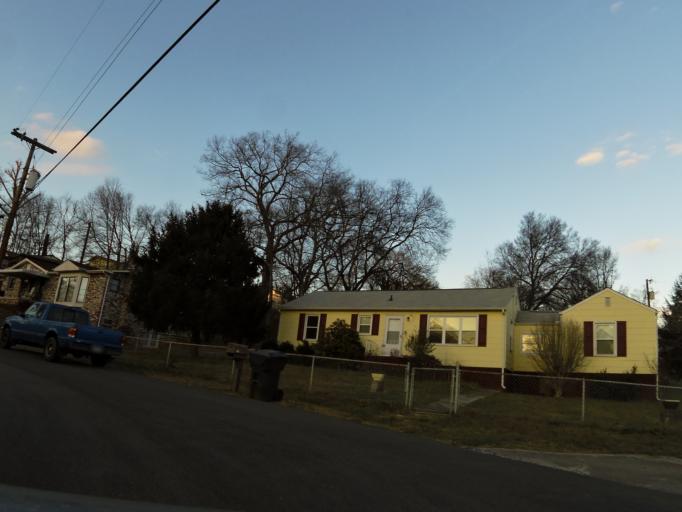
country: US
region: Tennessee
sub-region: Knox County
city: Knoxville
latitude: 35.9393
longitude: -83.9142
